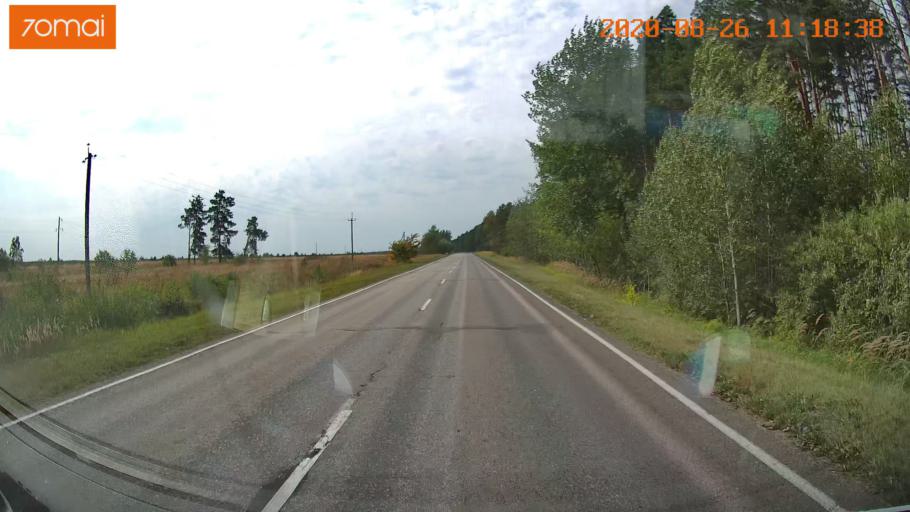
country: RU
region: Rjazan
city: Shilovo
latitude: 54.4079
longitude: 41.0938
